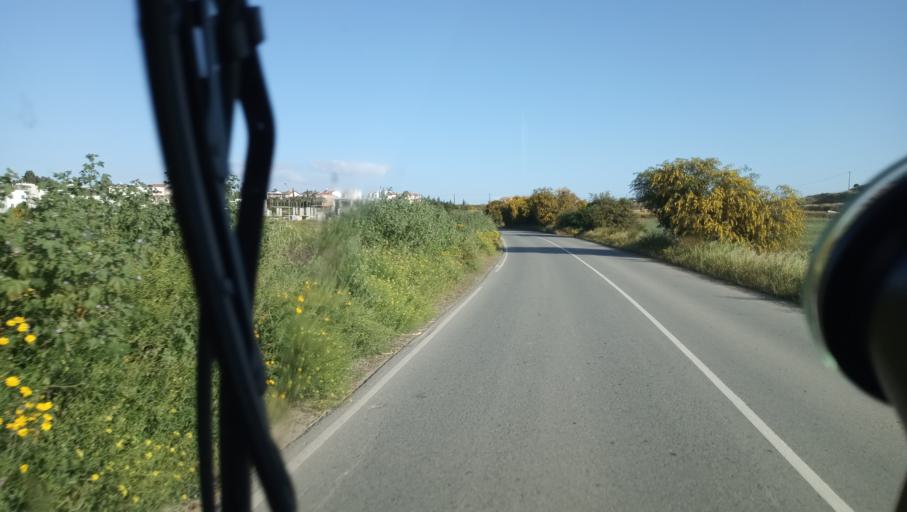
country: CY
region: Lefkosia
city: Geri
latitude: 35.0788
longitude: 33.3978
